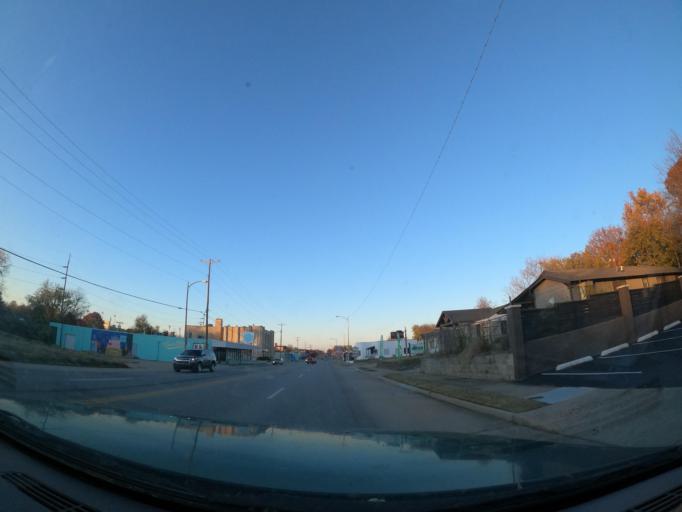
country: US
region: Oklahoma
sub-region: Tulsa County
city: Tulsa
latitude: 36.1448
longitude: -95.9403
